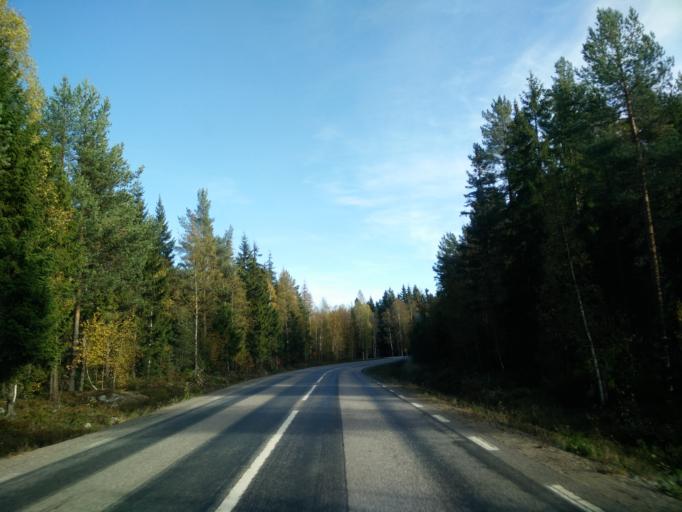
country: SE
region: Gaevleborg
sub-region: Hudiksvalls Kommun
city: Iggesund
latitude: 61.5518
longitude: 16.9870
